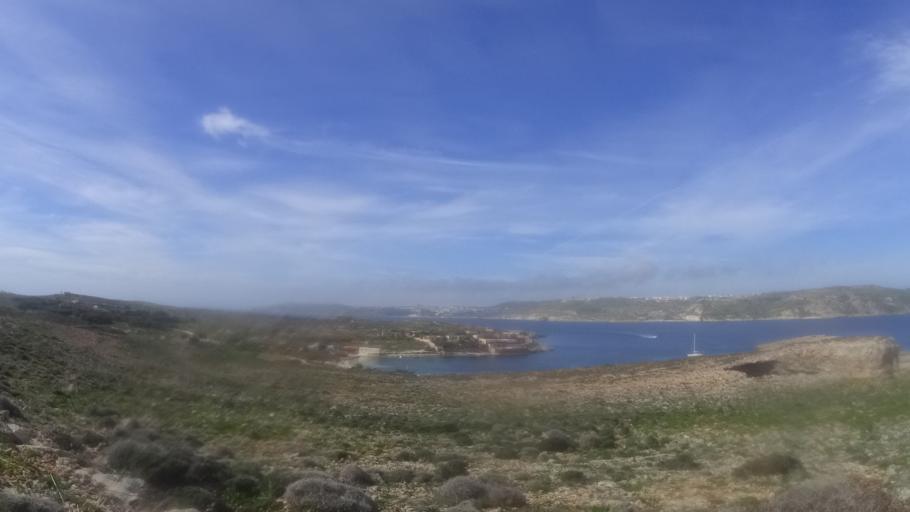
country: MT
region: Il-Qala
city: Qala
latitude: 36.0159
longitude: 14.3415
